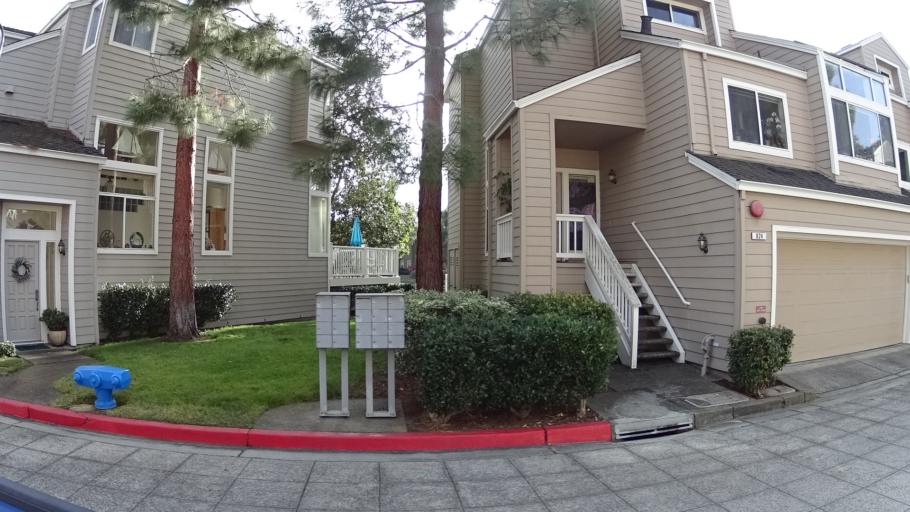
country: US
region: California
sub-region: San Mateo County
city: Redwood Shores
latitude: 37.5371
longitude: -122.2381
